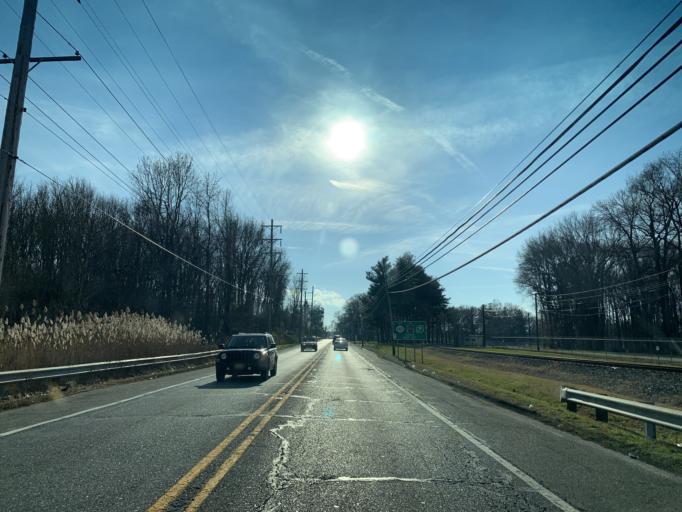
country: US
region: New Jersey
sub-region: Salem County
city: Carneys Point
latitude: 39.6895
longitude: -75.4867
